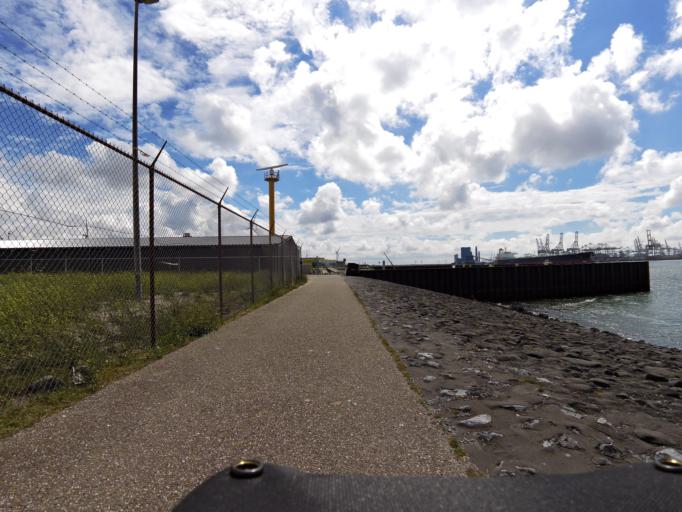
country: NL
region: South Holland
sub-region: Gemeente Rotterdam
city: Hoek van Holland
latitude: 51.9620
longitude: 4.0910
